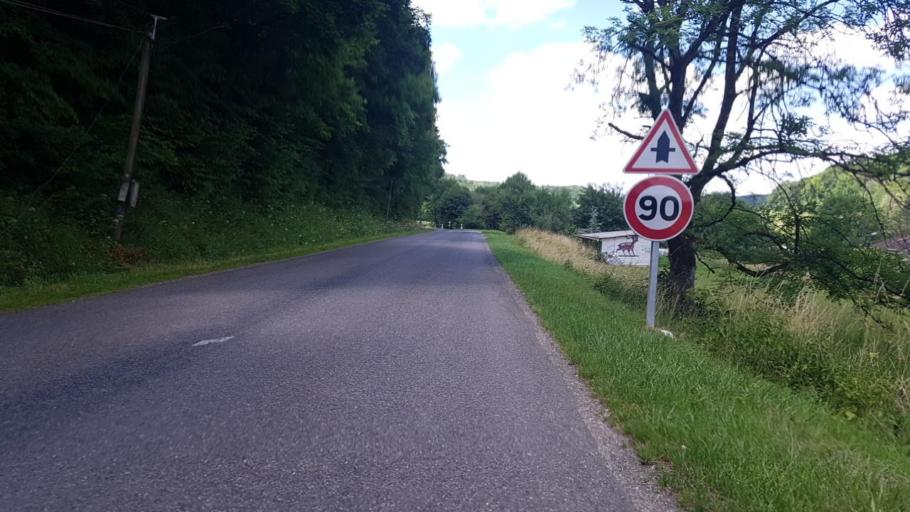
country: FR
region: Lorraine
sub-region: Departement de la Meuse
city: Gondrecourt-le-Chateau
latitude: 48.6312
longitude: 5.4635
